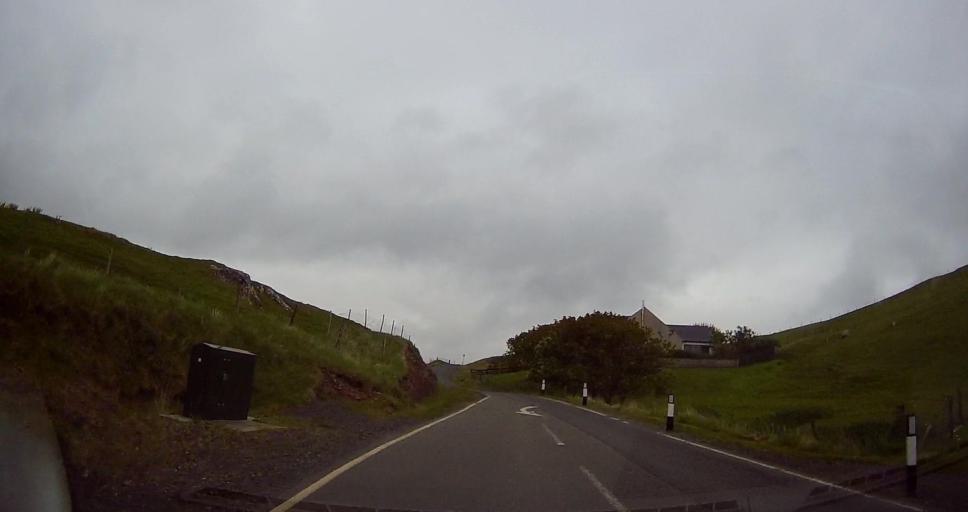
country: GB
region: Scotland
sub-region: Shetland Islands
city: Lerwick
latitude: 60.3758
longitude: -1.3847
